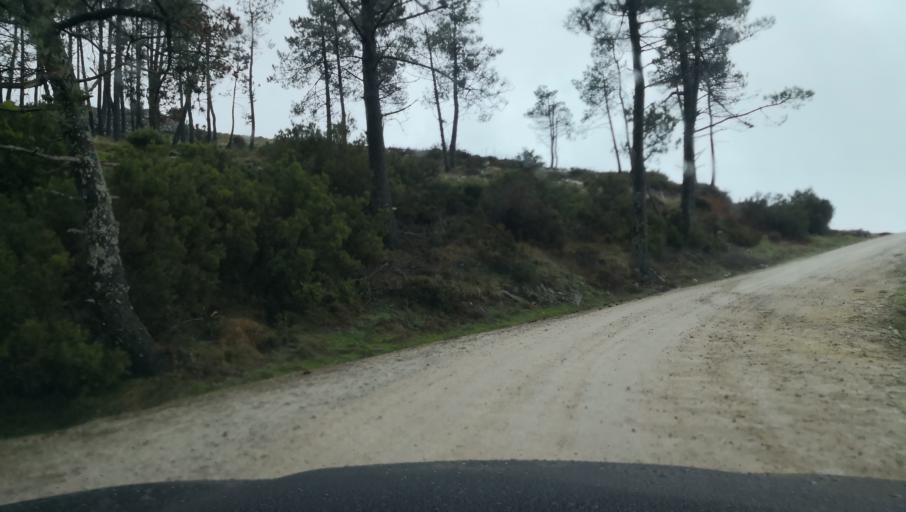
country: PT
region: Vila Real
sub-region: Vila Real
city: Vila Real
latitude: 41.3221
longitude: -7.8659
